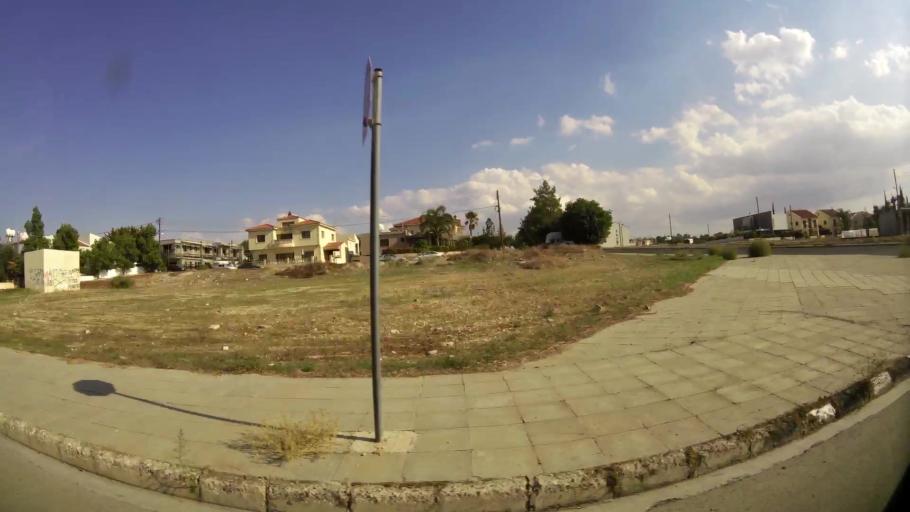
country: CY
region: Lefkosia
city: Kato Deftera
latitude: 35.1455
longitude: 33.2991
